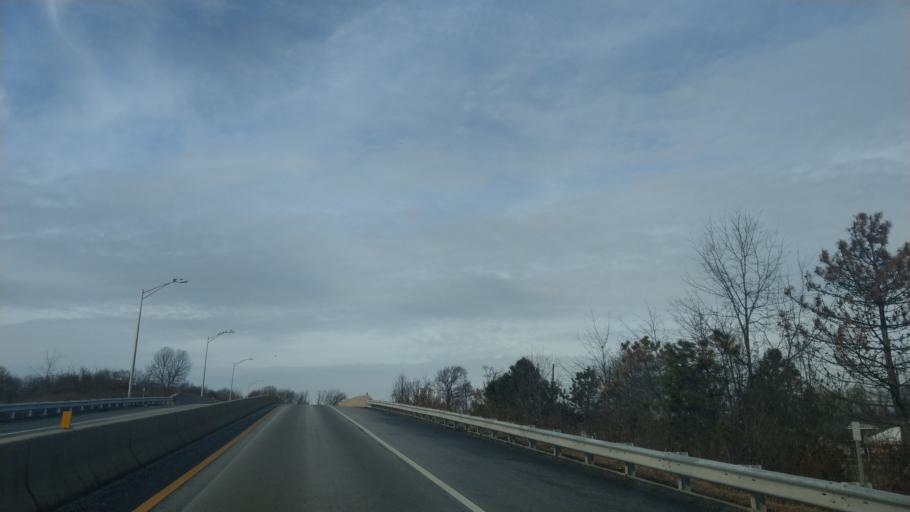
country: US
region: New Jersey
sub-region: Burlington County
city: Roebling
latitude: 40.1035
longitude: -74.7883
